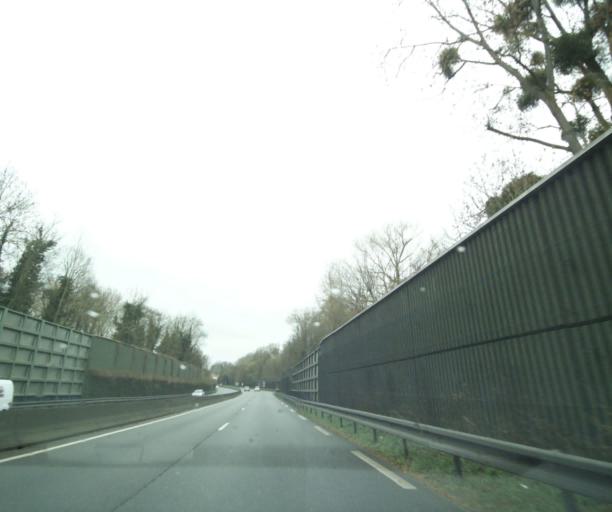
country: FR
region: Ile-de-France
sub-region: Departement de l'Essonne
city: Arpajon
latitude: 48.5902
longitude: 2.2375
